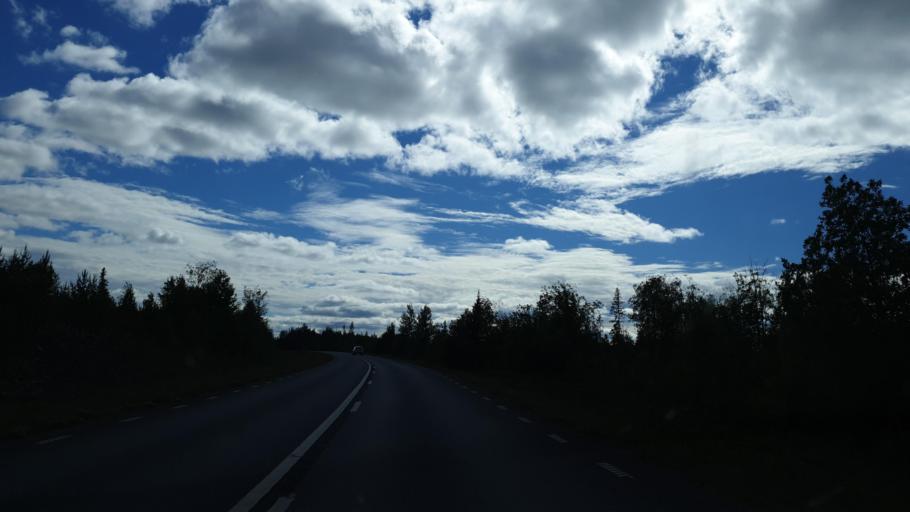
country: SE
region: Vaesterbotten
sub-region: Dorotea Kommun
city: Dorotea
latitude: 64.3203
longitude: 16.6135
